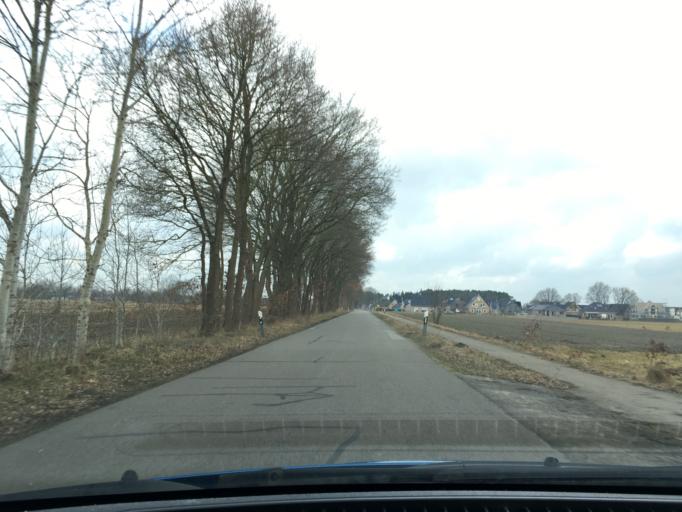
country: DE
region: Lower Saxony
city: Handorf
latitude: 53.3300
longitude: 10.3537
